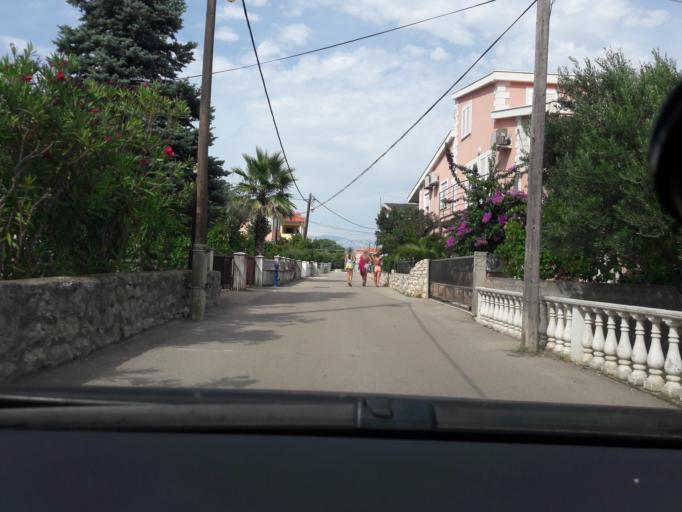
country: HR
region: Zadarska
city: Vir
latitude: 44.2998
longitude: 15.0823
